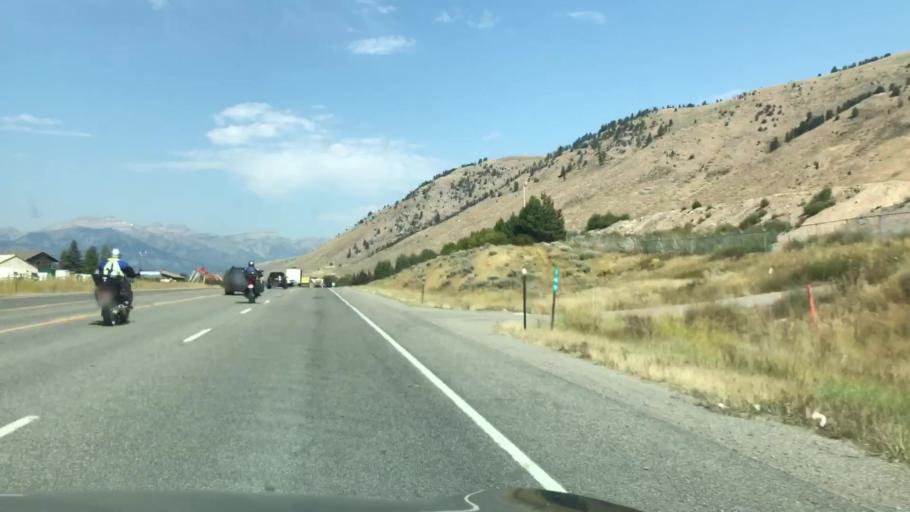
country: US
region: Wyoming
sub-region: Teton County
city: South Park
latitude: 43.4186
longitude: -110.7747
